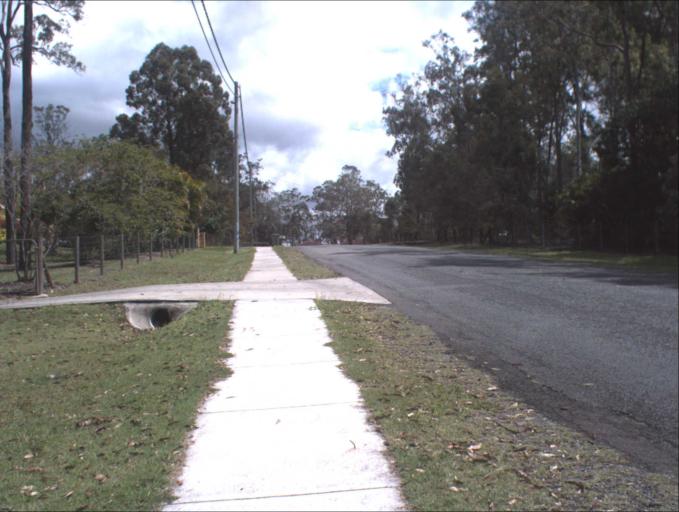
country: AU
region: Queensland
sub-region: Logan
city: Park Ridge South
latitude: -27.7441
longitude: 153.0197
